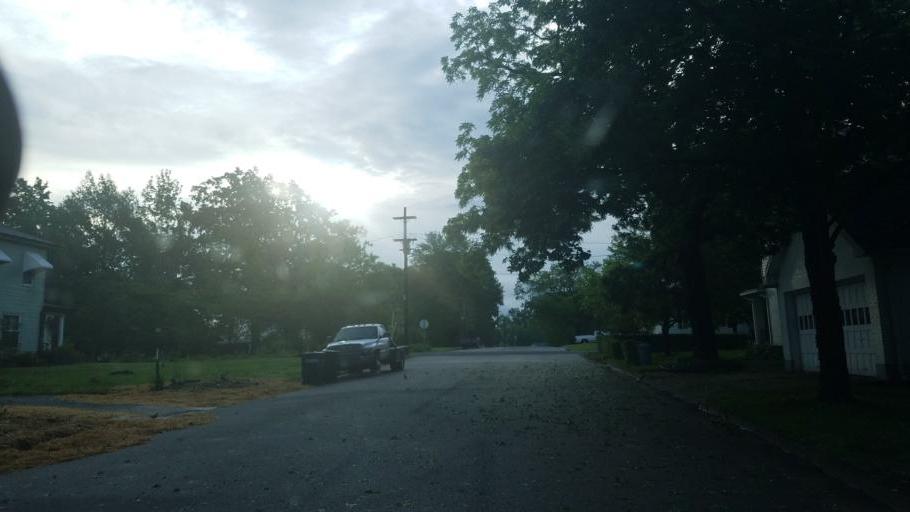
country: US
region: Missouri
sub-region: Moniteau County
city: California
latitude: 38.6248
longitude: -92.5700
